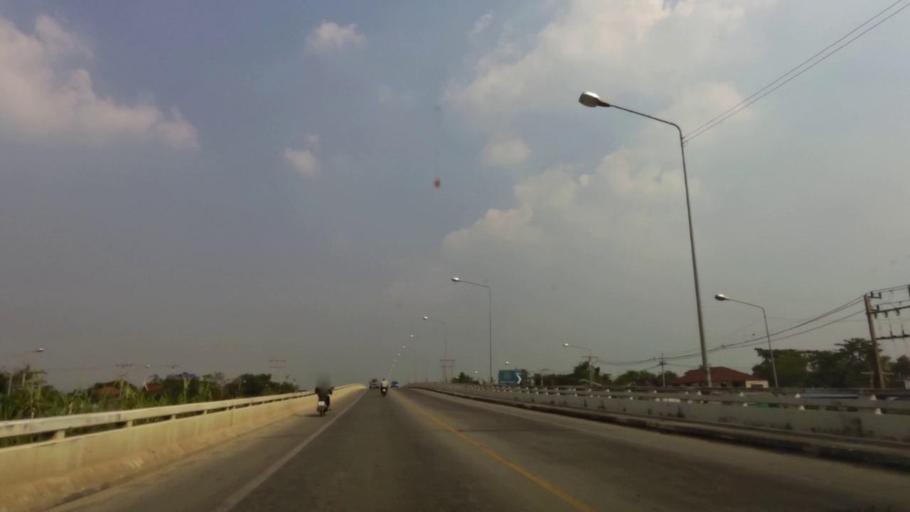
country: TH
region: Phra Nakhon Si Ayutthaya
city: Phra Nakhon Si Ayutthaya
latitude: 14.3048
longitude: 100.5627
